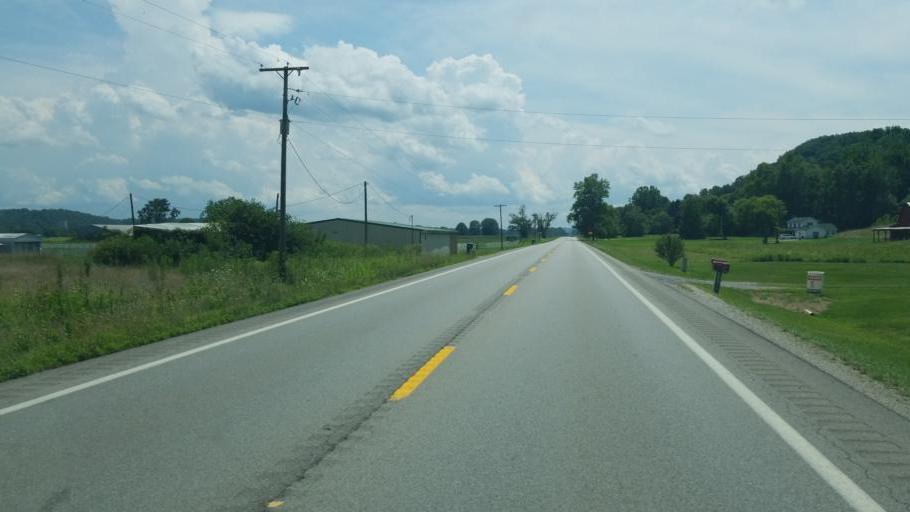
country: US
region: West Virginia
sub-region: Putnam County
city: Buffalo
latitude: 38.7071
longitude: -81.9671
